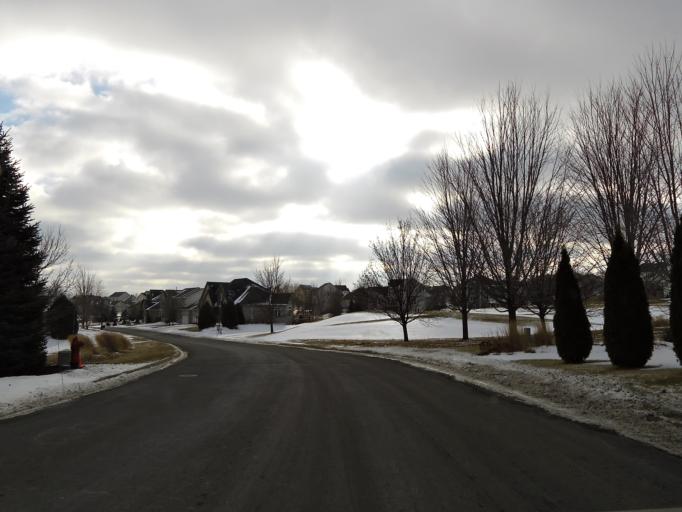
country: US
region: Minnesota
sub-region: Scott County
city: Prior Lake
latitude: 44.7303
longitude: -93.4544
